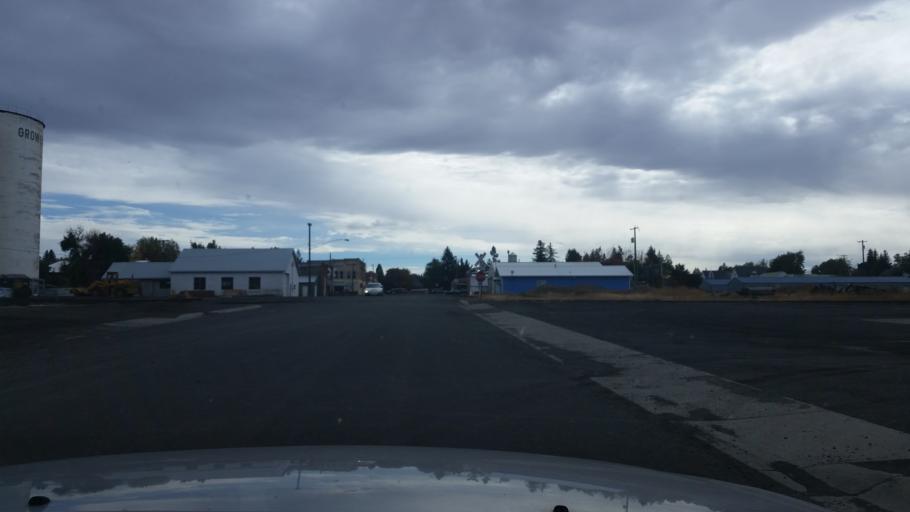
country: US
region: Washington
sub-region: Spokane County
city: Medical Lake
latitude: 47.6714
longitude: -117.8809
